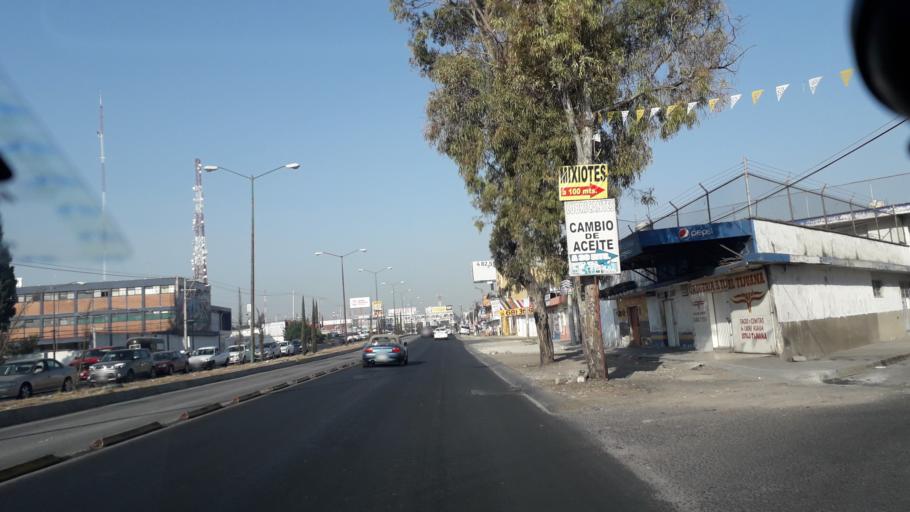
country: MX
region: Puebla
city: Tlazcalancingo
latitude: 19.0350
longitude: -98.2588
